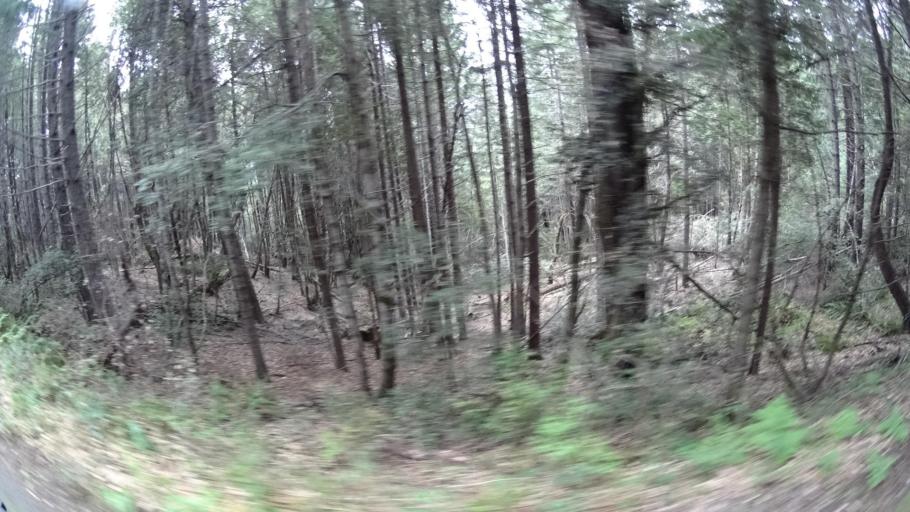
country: US
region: California
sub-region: Humboldt County
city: Willow Creek
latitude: 41.2021
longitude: -123.7726
